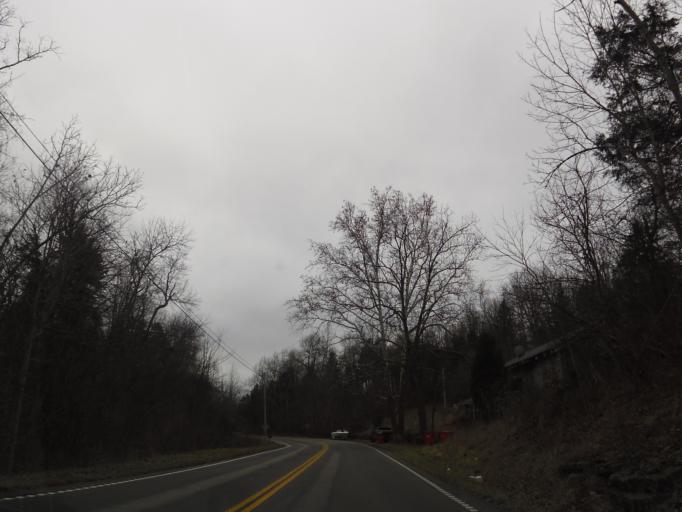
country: US
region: Kentucky
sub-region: Franklin County
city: Frankfort
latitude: 38.2331
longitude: -84.9172
